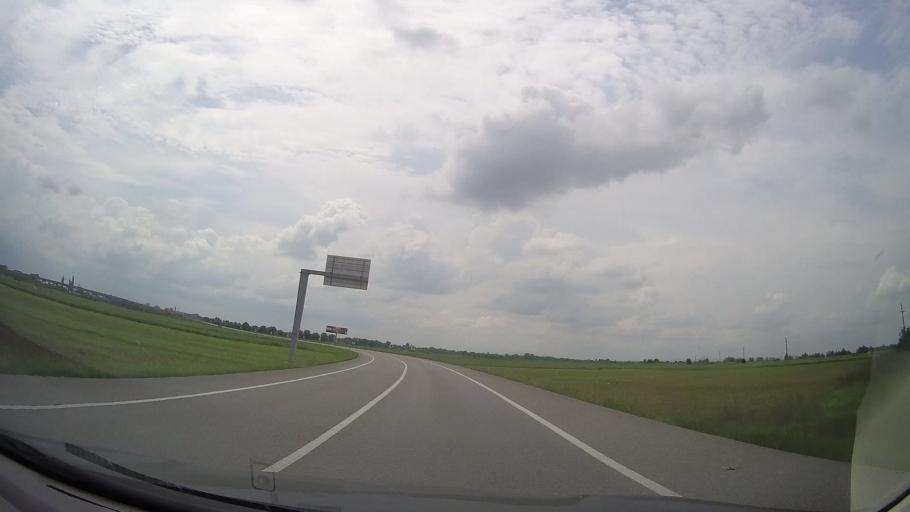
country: RO
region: Timis
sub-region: Comuna Costeiu
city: Costeiu
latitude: 45.7254
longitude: 21.8698
